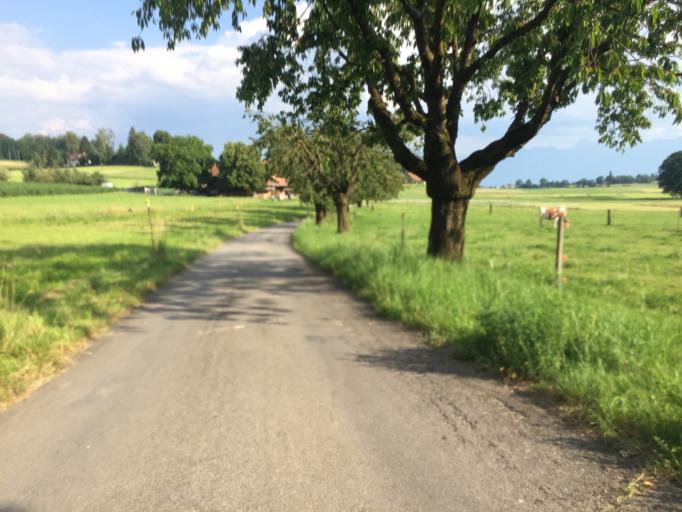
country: CH
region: Bern
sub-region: Bern-Mittelland District
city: Rubigen
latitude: 46.9011
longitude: 7.5705
